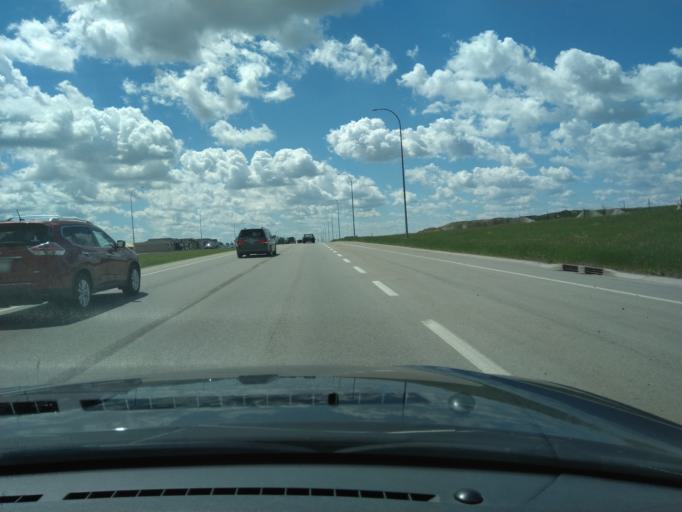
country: CA
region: Alberta
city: Calgary
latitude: 51.1369
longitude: -113.9703
